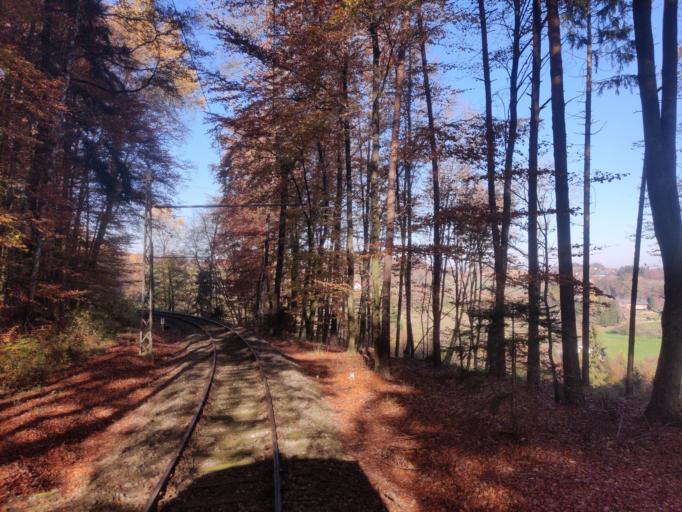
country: AT
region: Styria
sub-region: Politischer Bezirk Suedoststeiermark
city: Maierdorf
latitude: 46.9277
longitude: 15.8548
